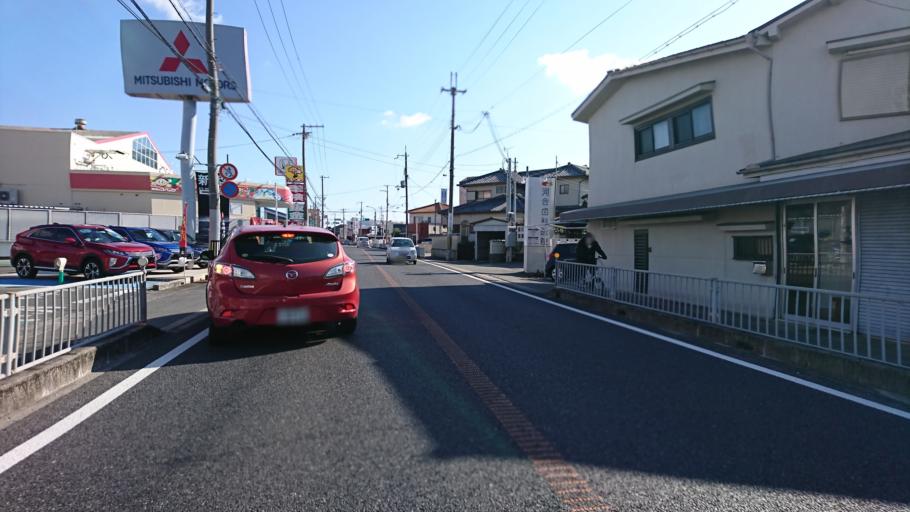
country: JP
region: Hyogo
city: Kakogawacho-honmachi
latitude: 34.7781
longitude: 134.8209
